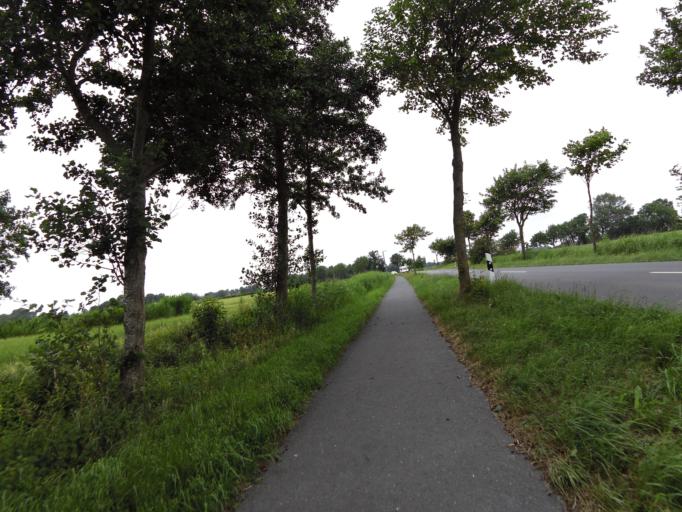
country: DE
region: Lower Saxony
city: Padingbuttel
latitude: 53.7157
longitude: 8.5488
